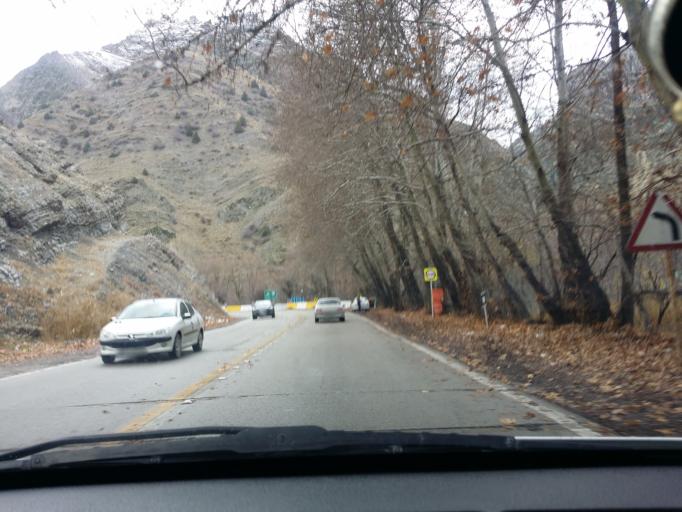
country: IR
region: Tehran
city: Tajrish
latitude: 36.0253
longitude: 51.2477
